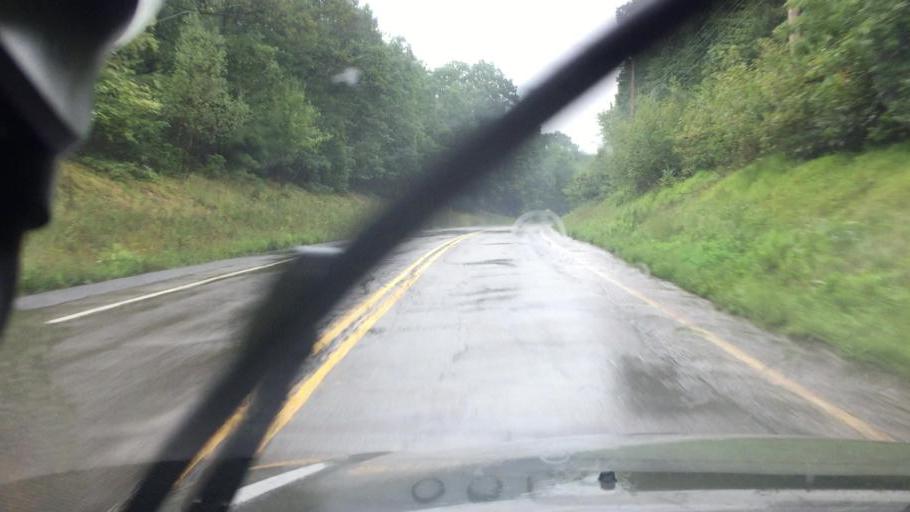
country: US
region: Pennsylvania
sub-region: Luzerne County
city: White Haven
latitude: 41.0418
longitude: -75.8310
